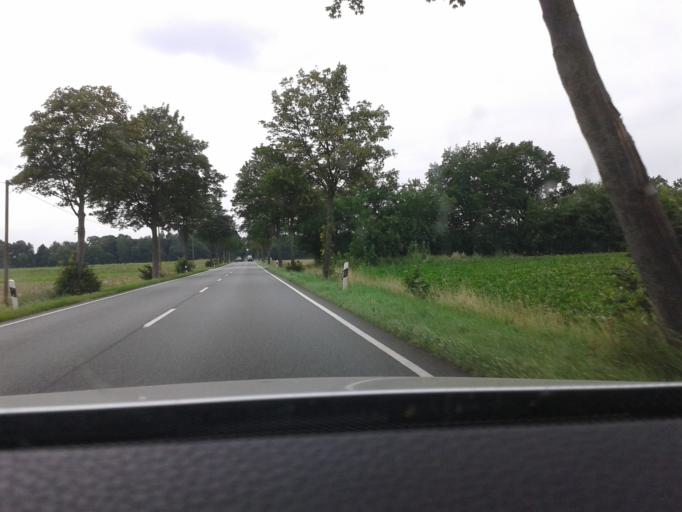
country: DE
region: Lower Saxony
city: Haenigsen
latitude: 52.4574
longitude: 10.1201
